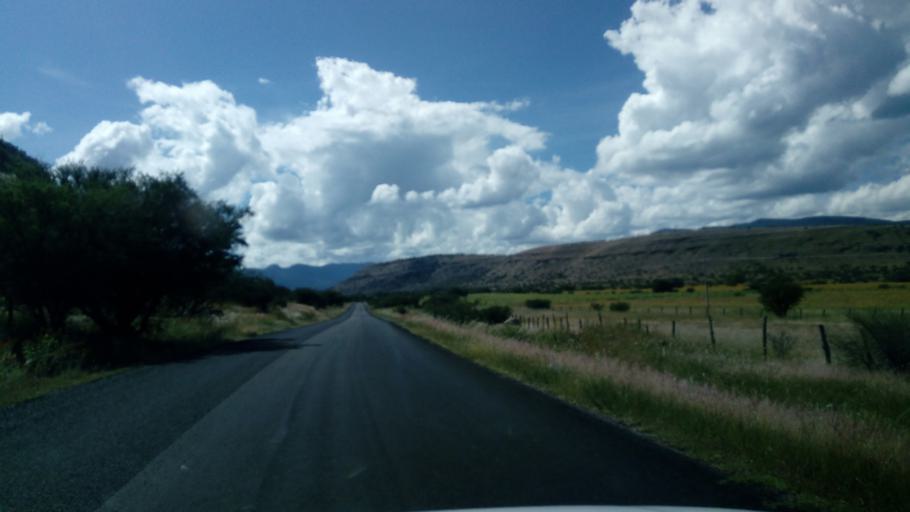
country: MX
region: Durango
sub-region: Durango
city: Jose Refugio Salcido
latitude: 23.8327
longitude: -104.4811
